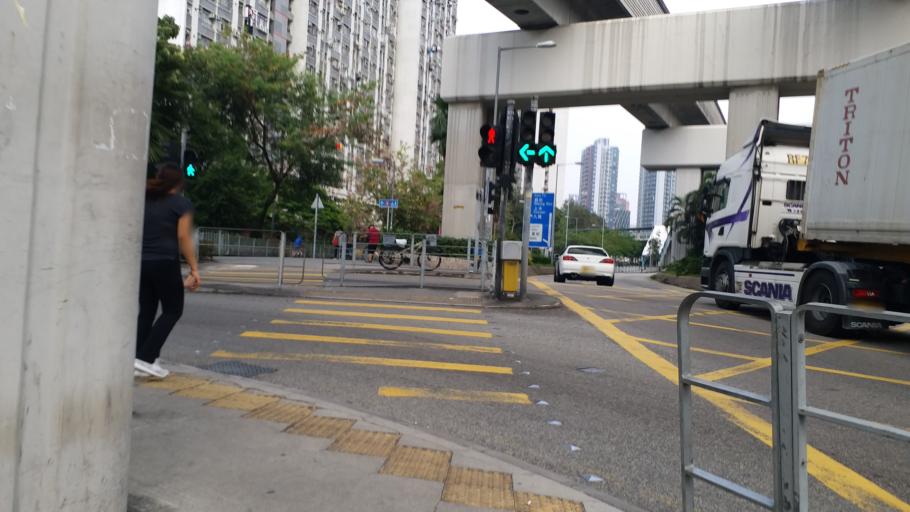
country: HK
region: Yuen Long
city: Yuen Long Kau Hui
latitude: 22.4477
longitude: 114.0215
